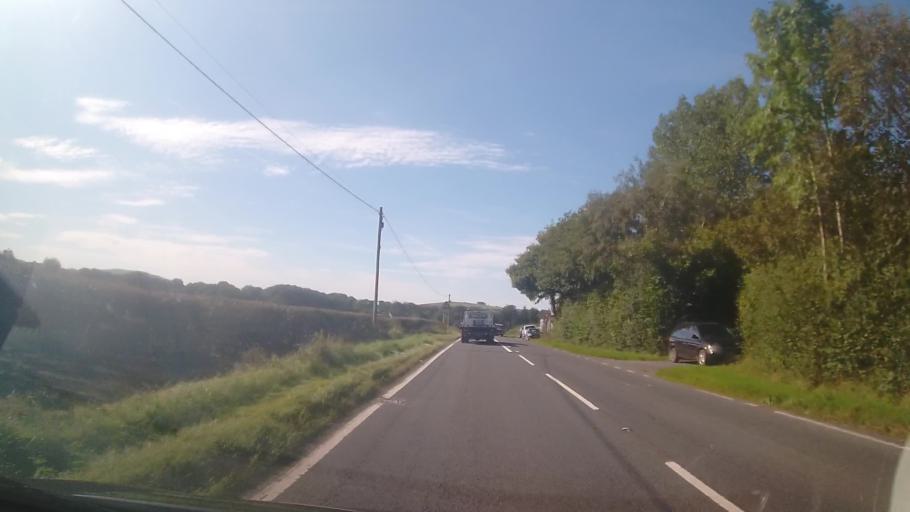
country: GB
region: Wales
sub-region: Sir Powys
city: Llandrindod Wells
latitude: 52.2806
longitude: -3.3651
